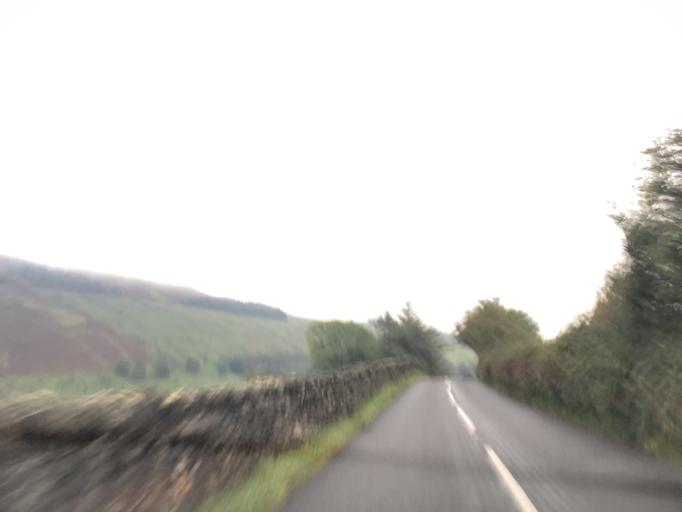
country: GB
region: England
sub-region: Cumbria
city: Windermere
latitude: 54.4298
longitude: -2.9031
